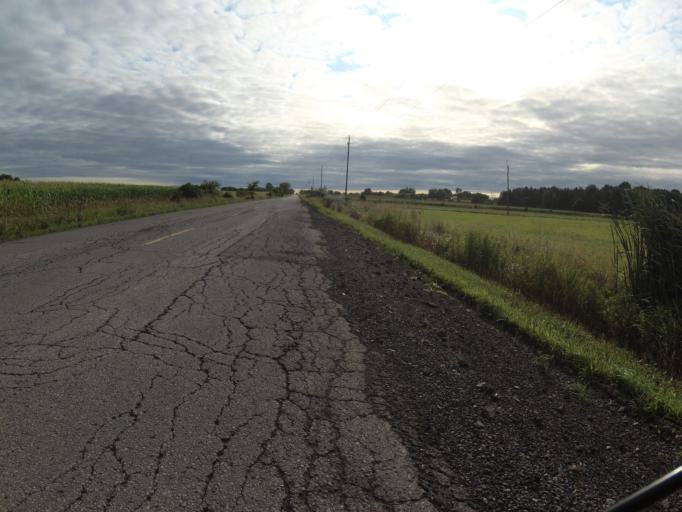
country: CA
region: Ontario
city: Clarence-Rockland
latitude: 45.3201
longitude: -75.3984
